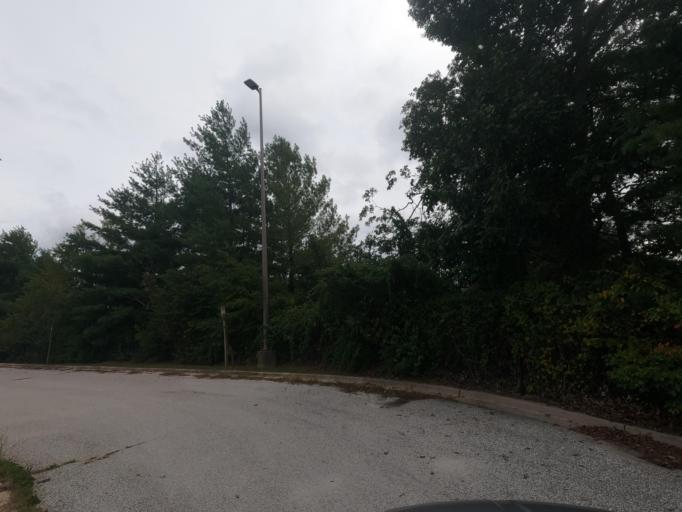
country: US
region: Maryland
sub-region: Charles County
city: Waldorf
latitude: 38.6239
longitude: -76.8724
